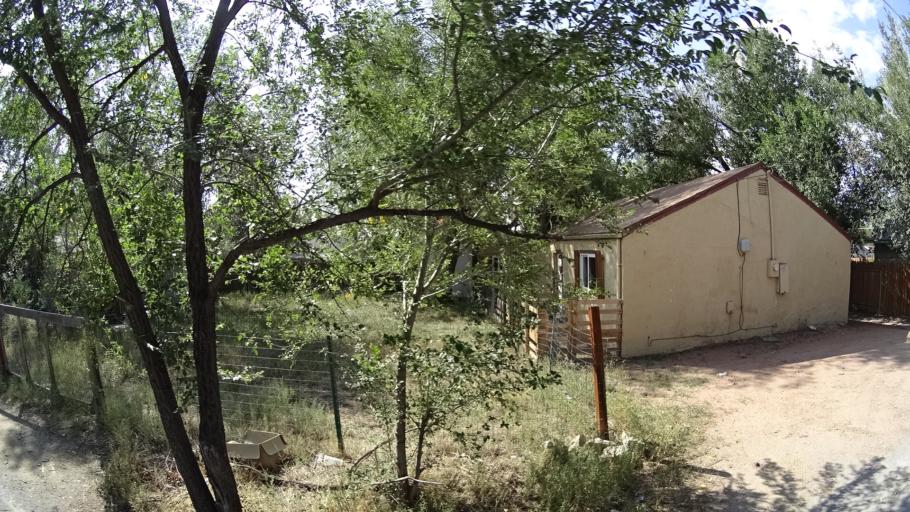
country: US
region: Colorado
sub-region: El Paso County
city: Colorado Springs
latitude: 38.8245
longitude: -104.8029
